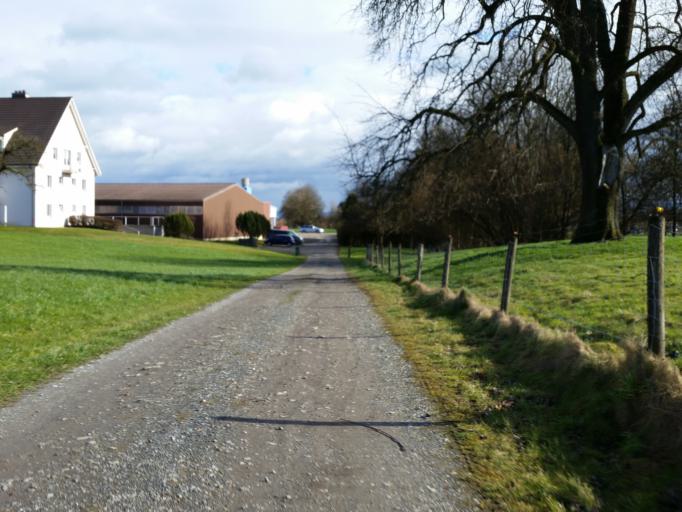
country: CH
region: Thurgau
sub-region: Arbon District
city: Salmsach
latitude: 47.5494
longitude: 9.3695
